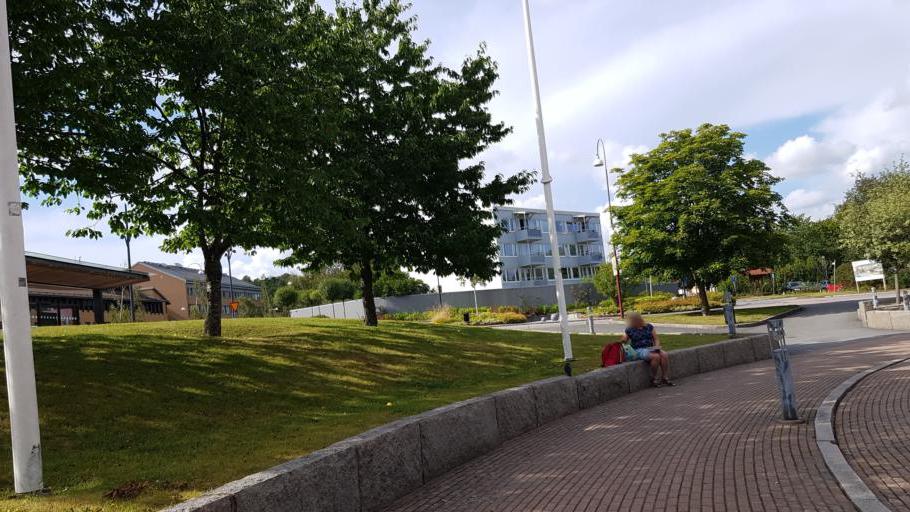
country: SE
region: Vaestra Goetaland
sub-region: Harryda Kommun
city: Molnlycke
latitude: 57.6592
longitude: 12.1183
